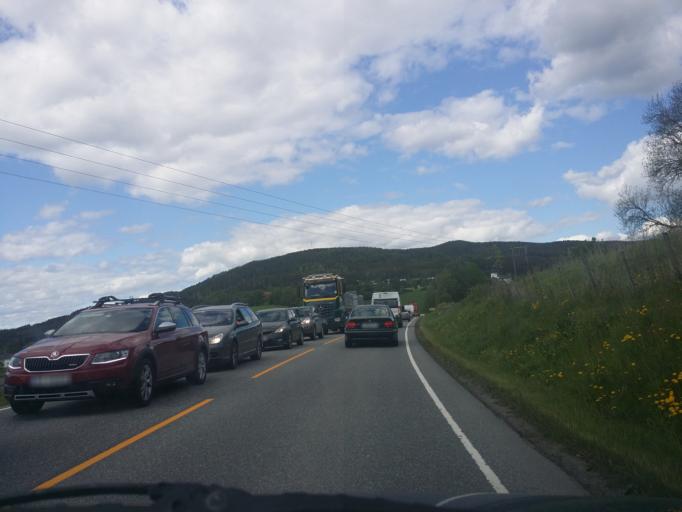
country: NO
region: Oppland
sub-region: Jevnaker
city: Jevnaker
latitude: 60.2499
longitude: 10.4261
